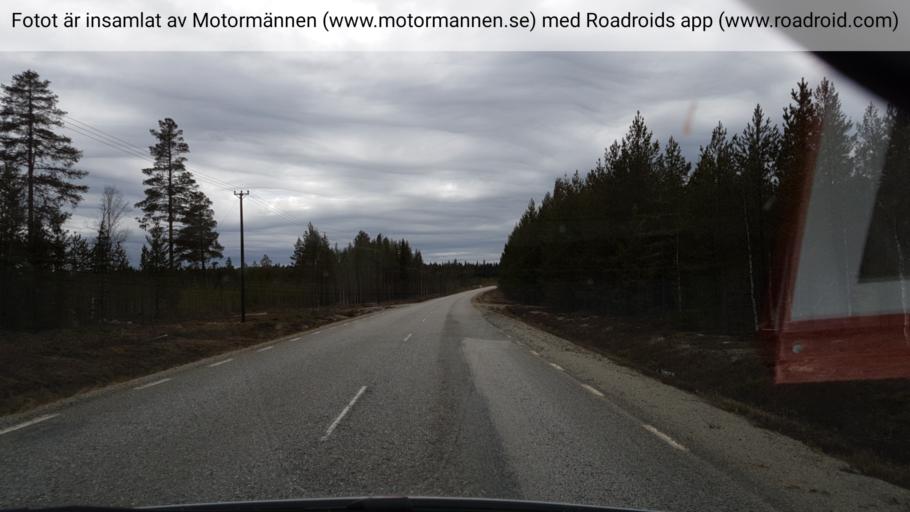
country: SE
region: Vaesterbotten
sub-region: Asele Kommun
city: Asele
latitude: 63.9206
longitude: 17.2495
